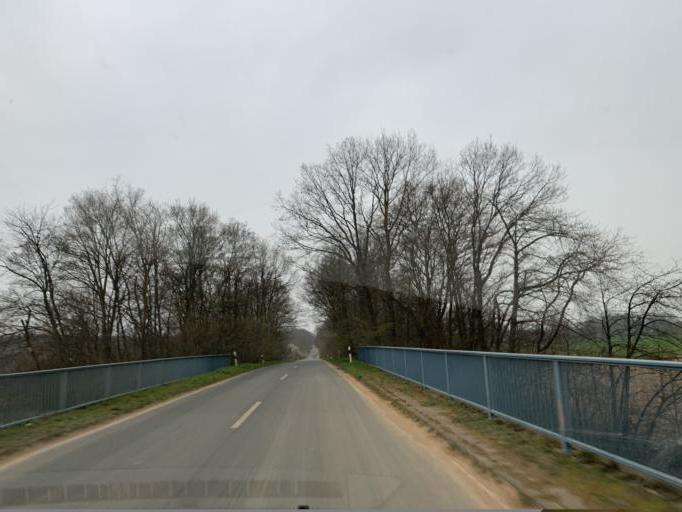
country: DE
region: North Rhine-Westphalia
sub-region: Regierungsbezirk Koln
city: Elsdorf
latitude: 50.8912
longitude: 6.5917
